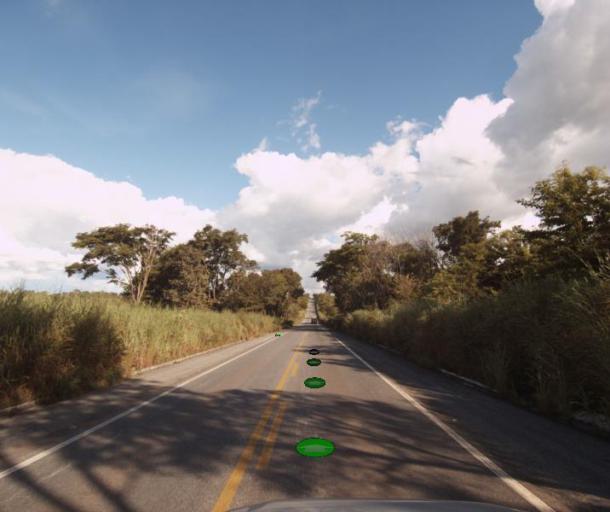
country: BR
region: Goias
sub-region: Porangatu
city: Porangatu
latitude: -13.1594
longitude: -49.1791
